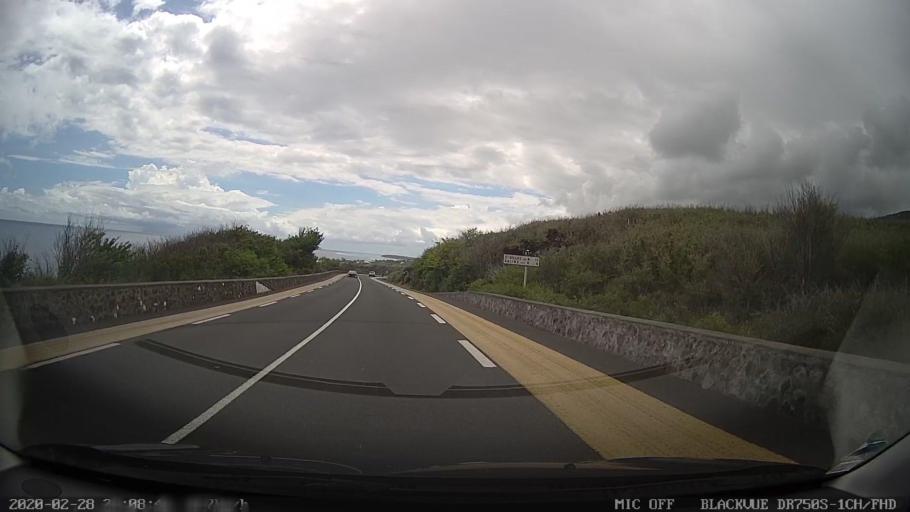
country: RE
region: Reunion
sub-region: Reunion
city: Saint-Leu
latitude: -21.1318
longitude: 55.2716
